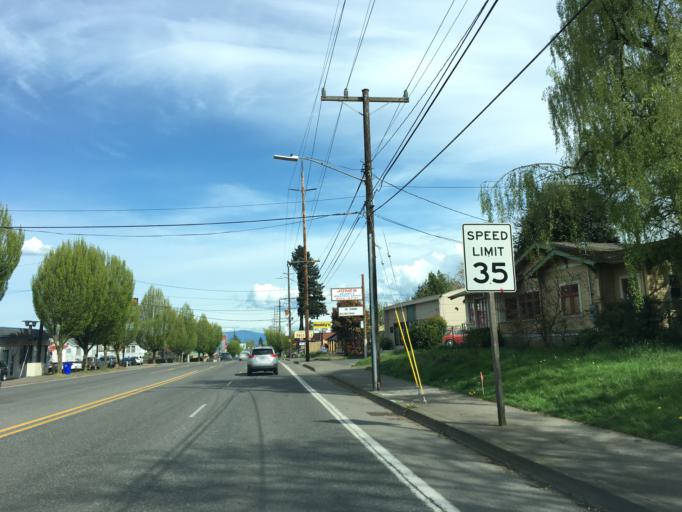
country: US
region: Oregon
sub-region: Multnomah County
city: Lents
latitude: 45.5581
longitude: -122.5471
